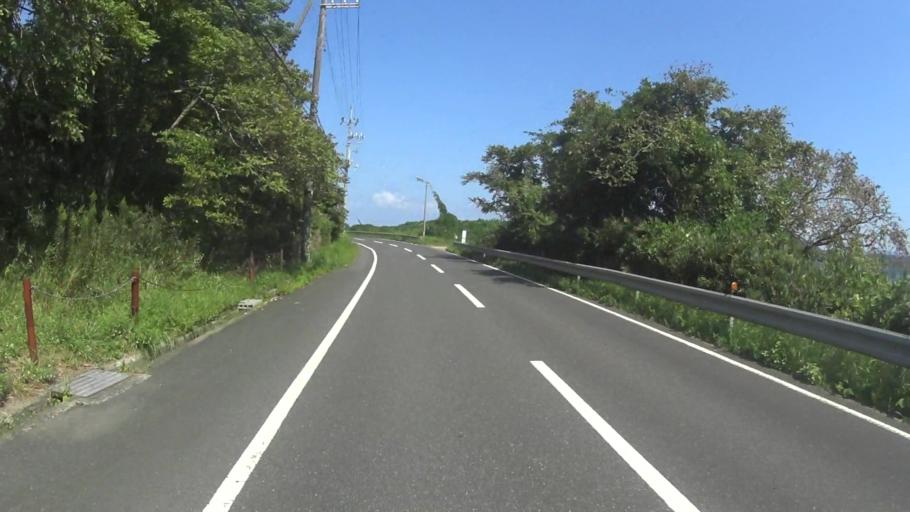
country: JP
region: Kyoto
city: Miyazu
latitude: 35.5929
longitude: 135.2111
